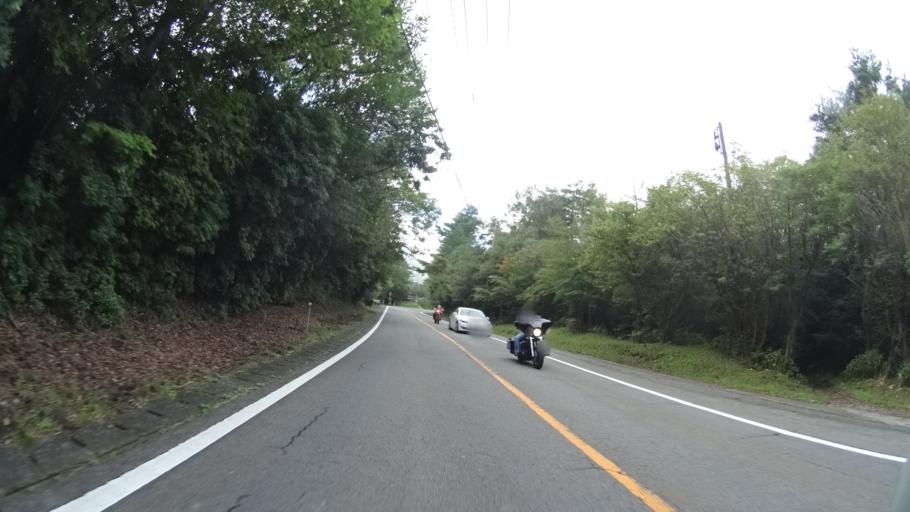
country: JP
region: Oita
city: Tsukawaki
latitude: 33.1149
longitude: 131.2274
